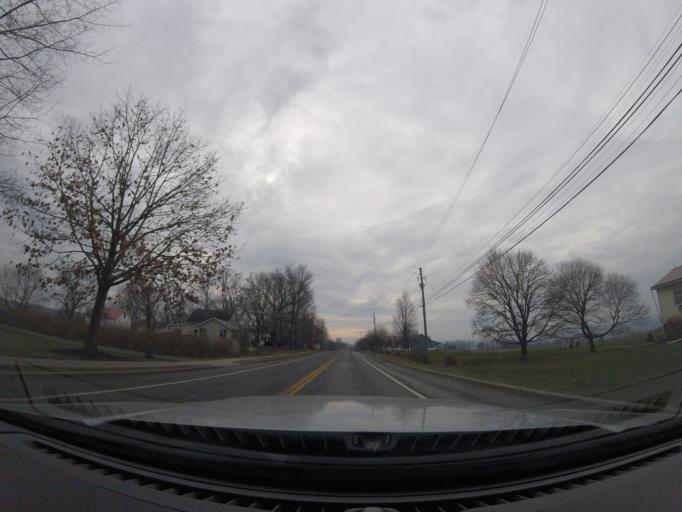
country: US
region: New York
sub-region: Schuyler County
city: Watkins Glen
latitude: 42.4133
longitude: -76.8510
